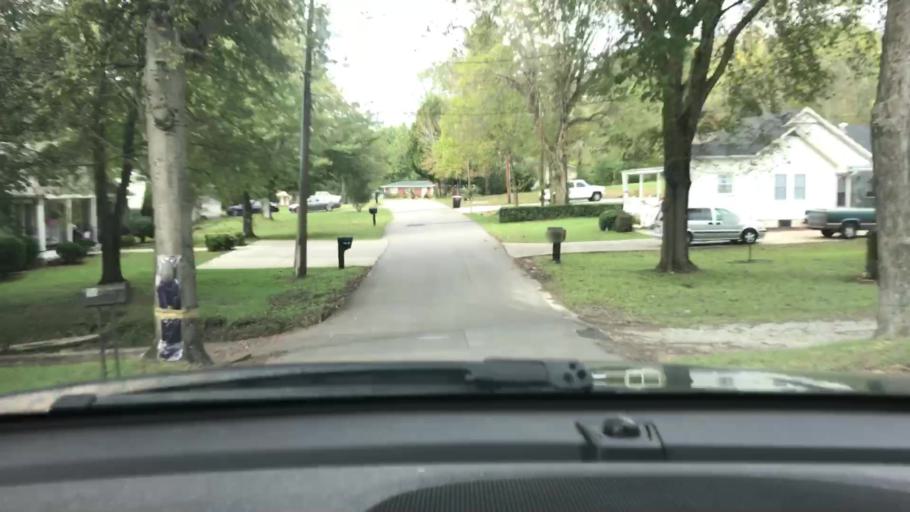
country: US
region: Tennessee
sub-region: Cheatham County
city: Ashland City
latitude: 36.2665
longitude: -87.0578
